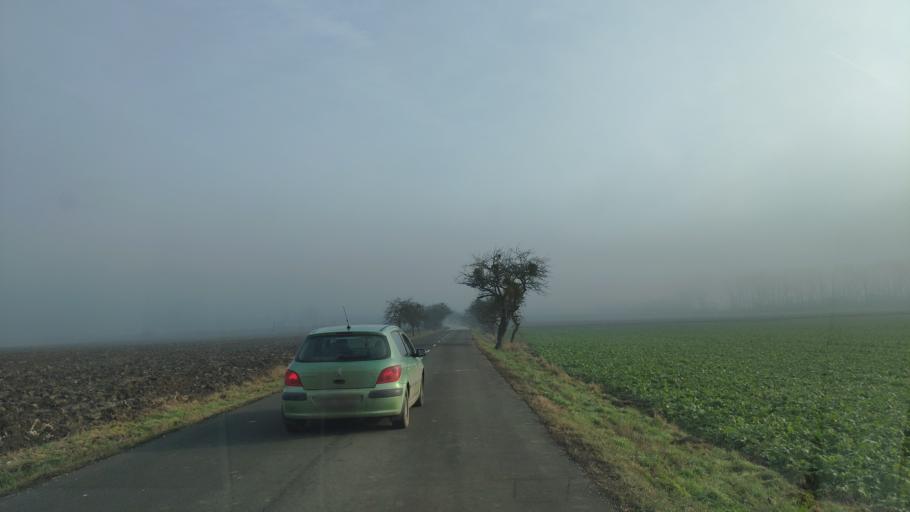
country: SK
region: Kosicky
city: Kosice
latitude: 48.7094
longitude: 21.4216
